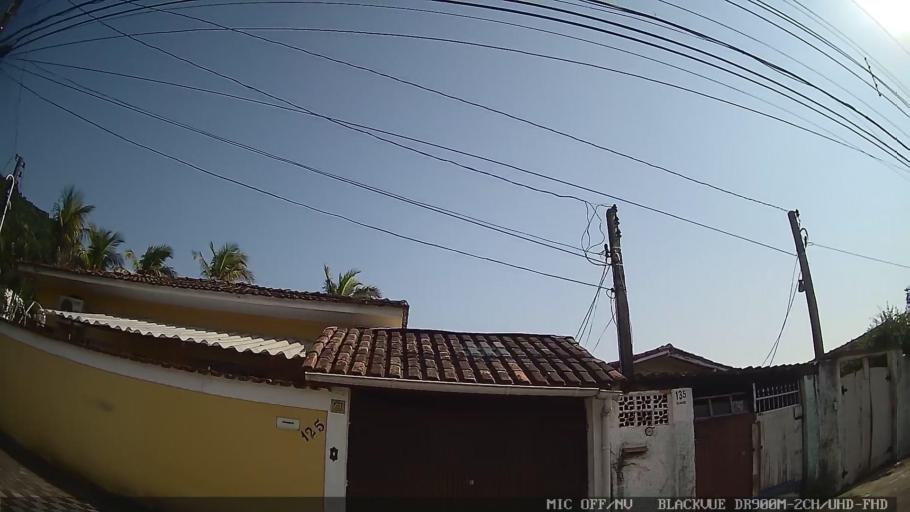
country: BR
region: Sao Paulo
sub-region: Guaruja
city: Guaruja
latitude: -23.9914
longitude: -46.2625
